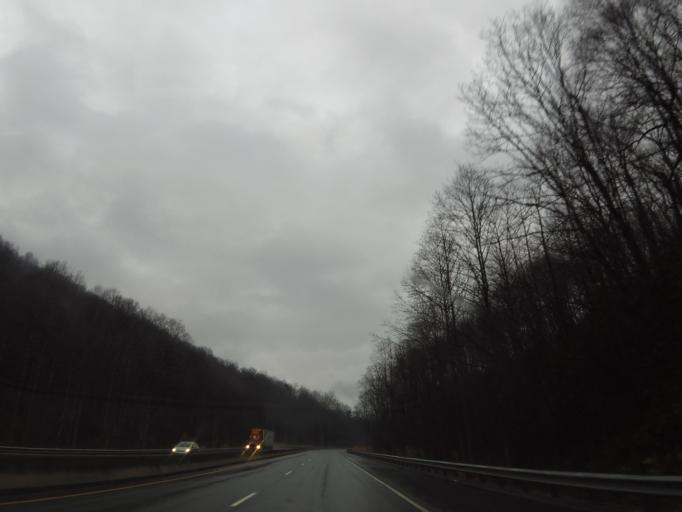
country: US
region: North Carolina
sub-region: Henderson County
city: Flat Rock
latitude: 35.1725
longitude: -82.4603
